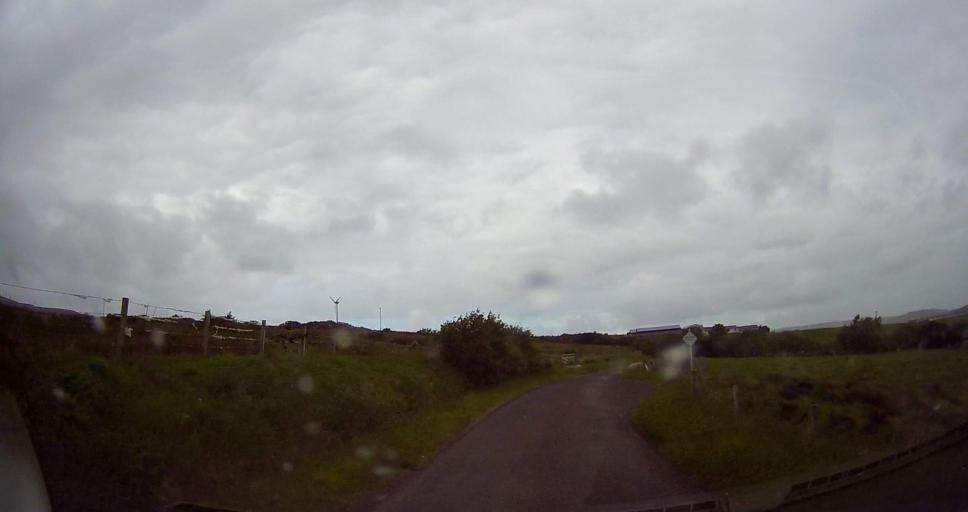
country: GB
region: Scotland
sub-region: Orkney Islands
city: Stromness
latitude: 58.9088
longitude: -3.3199
